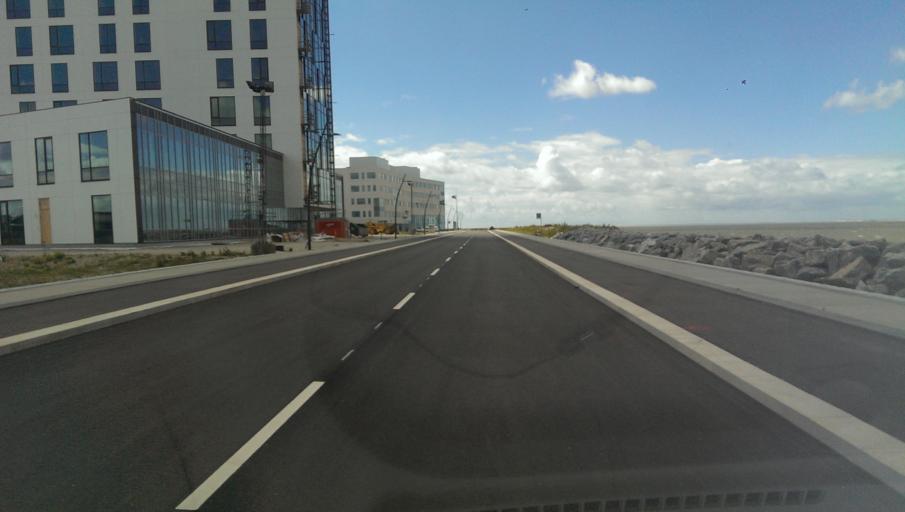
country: DK
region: South Denmark
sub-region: Fano Kommune
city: Nordby
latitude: 55.4818
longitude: 8.4134
